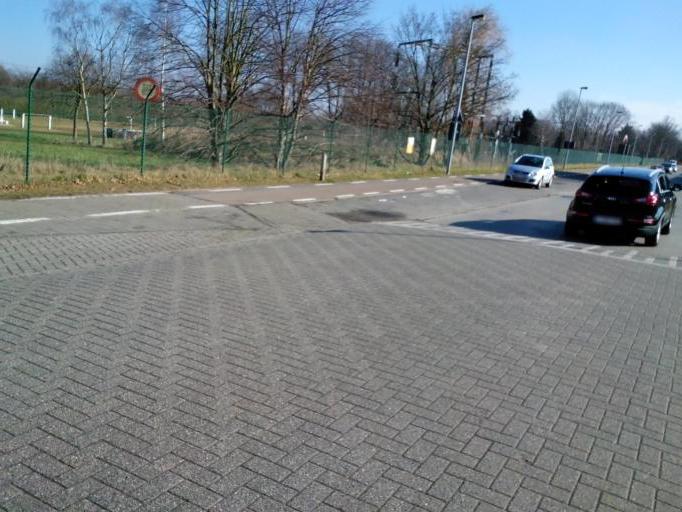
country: BE
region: Flanders
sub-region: Provincie Vlaams-Brabant
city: Leuven
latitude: 50.8561
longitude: 4.7052
